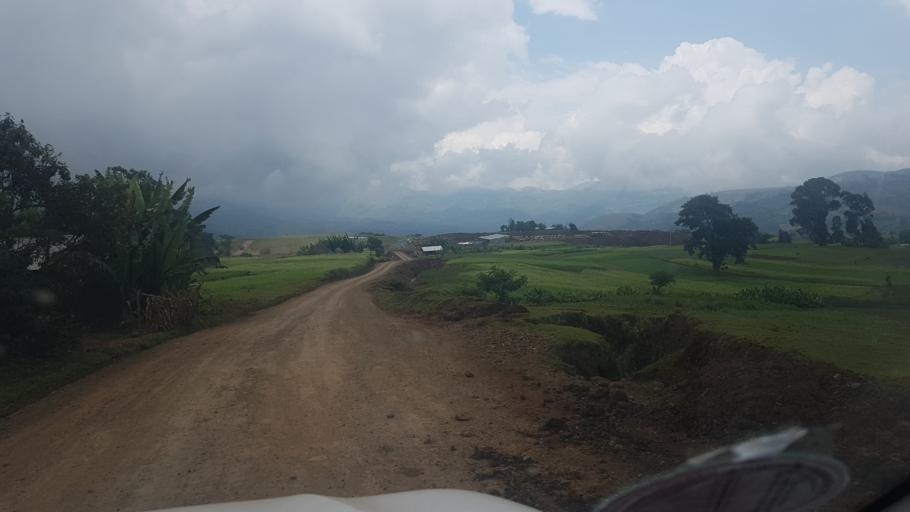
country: ET
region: Southern Nations, Nationalities, and People's Region
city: Arba Minch'
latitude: 6.3263
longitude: 37.5454
